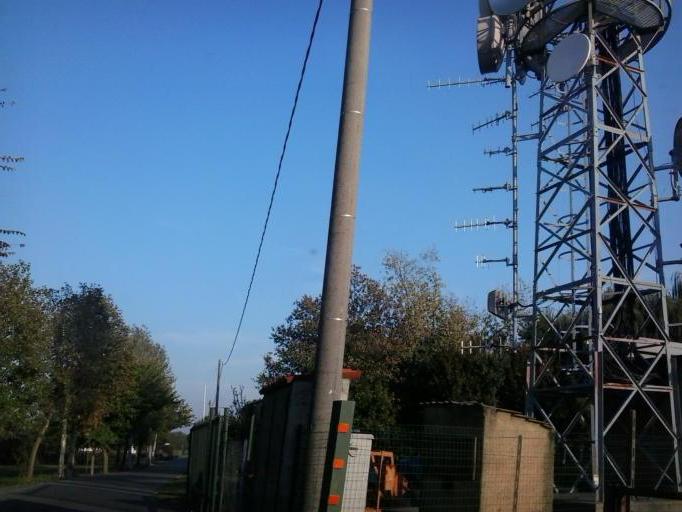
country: IT
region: Lombardy
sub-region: Provincia di Brescia
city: Capriano del Colle
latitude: 45.4683
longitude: 10.1453
